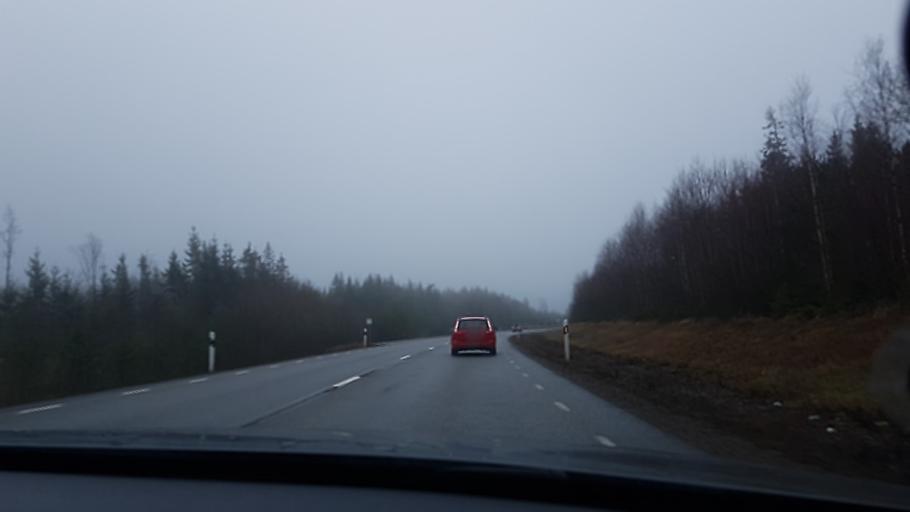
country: SE
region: Vaestra Goetaland
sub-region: Gullspangs Kommun
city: Gullspang
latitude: 58.8705
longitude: 14.0087
